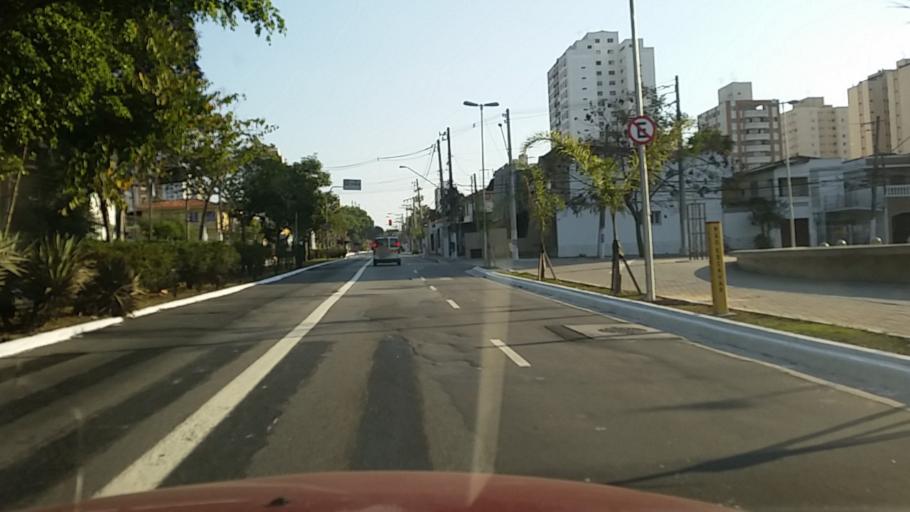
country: BR
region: Sao Paulo
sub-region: Diadema
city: Diadema
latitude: -23.6276
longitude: -46.6883
